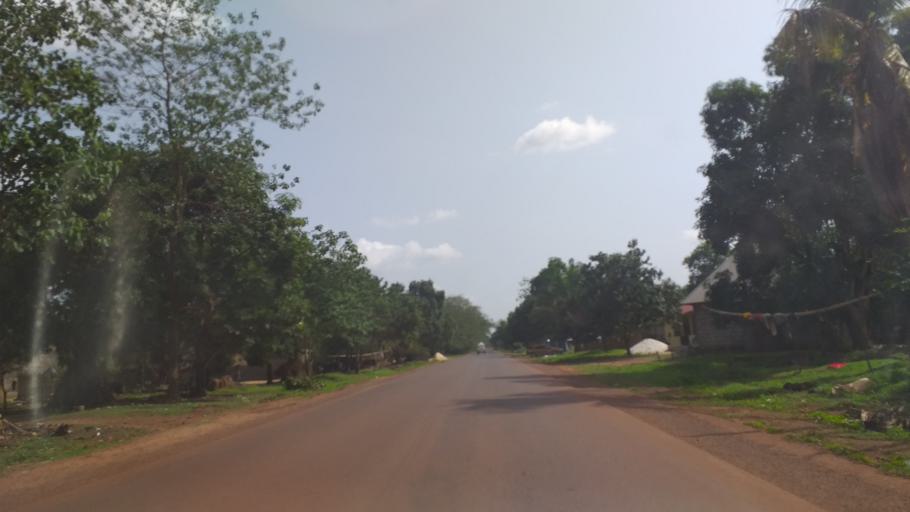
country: GN
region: Boke
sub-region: Boke Prefecture
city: Sangueya
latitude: 10.8209
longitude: -14.3746
